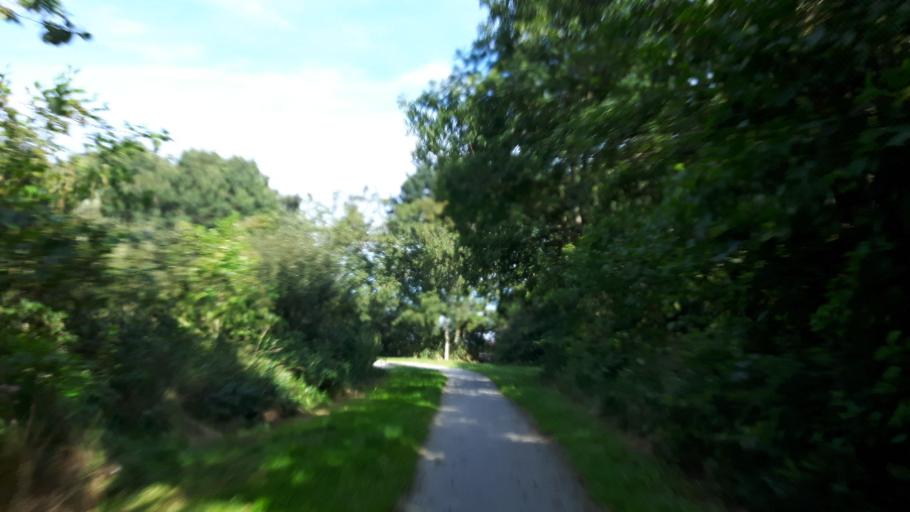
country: NL
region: Friesland
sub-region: Gemeente Skarsterlan
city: Joure
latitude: 52.9877
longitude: 5.7707
